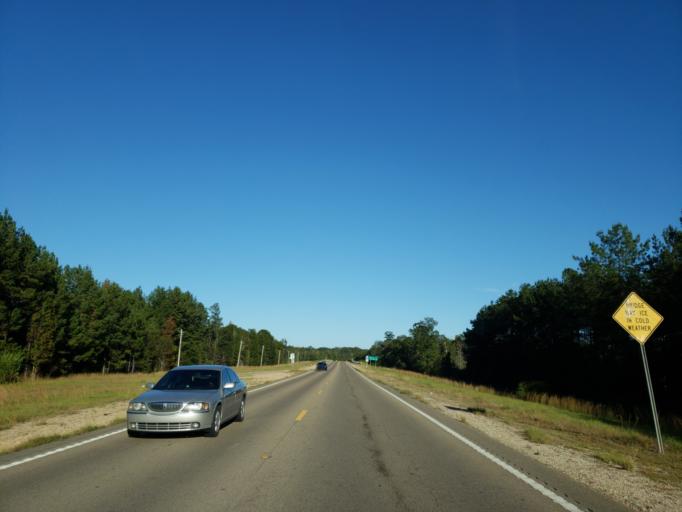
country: US
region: Mississippi
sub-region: Perry County
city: Richton
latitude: 31.3554
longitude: -88.9279
